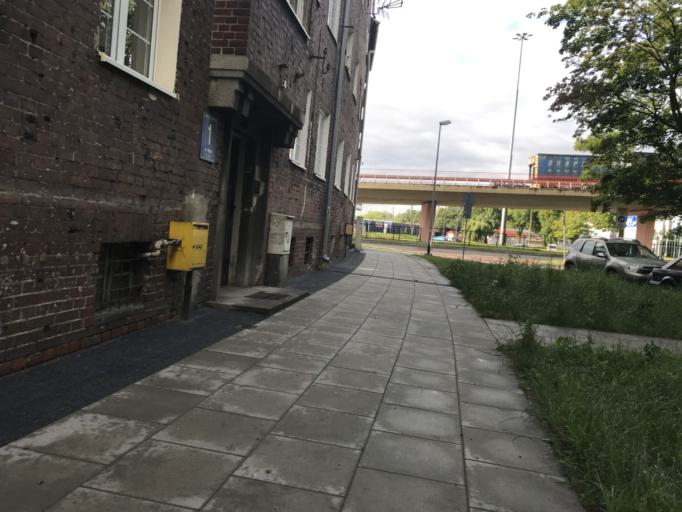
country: PL
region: Pomeranian Voivodeship
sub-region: Gdansk
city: Gdansk
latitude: 54.3495
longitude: 18.6715
